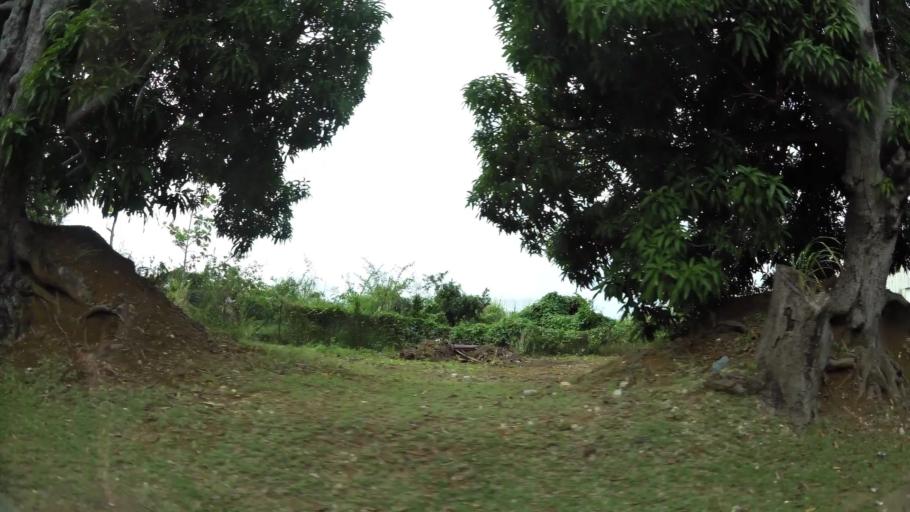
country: GP
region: Guadeloupe
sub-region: Guadeloupe
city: Baie-Mahault
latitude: 16.2566
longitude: -61.5982
